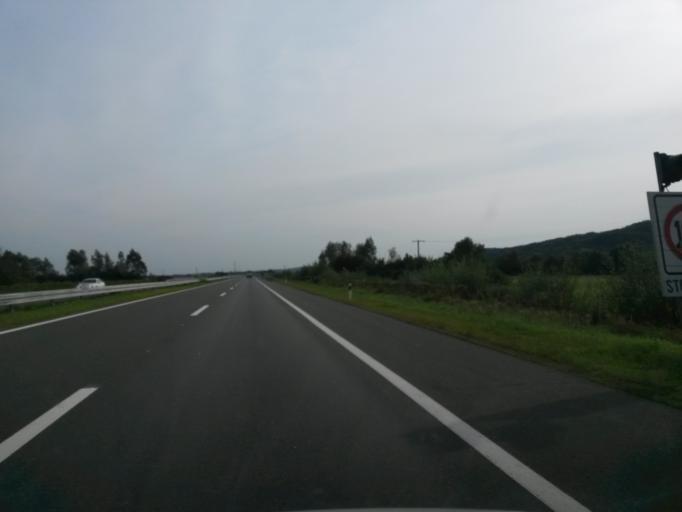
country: HR
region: Zagrebacka
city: Brckovljani
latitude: 45.9305
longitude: 16.2707
